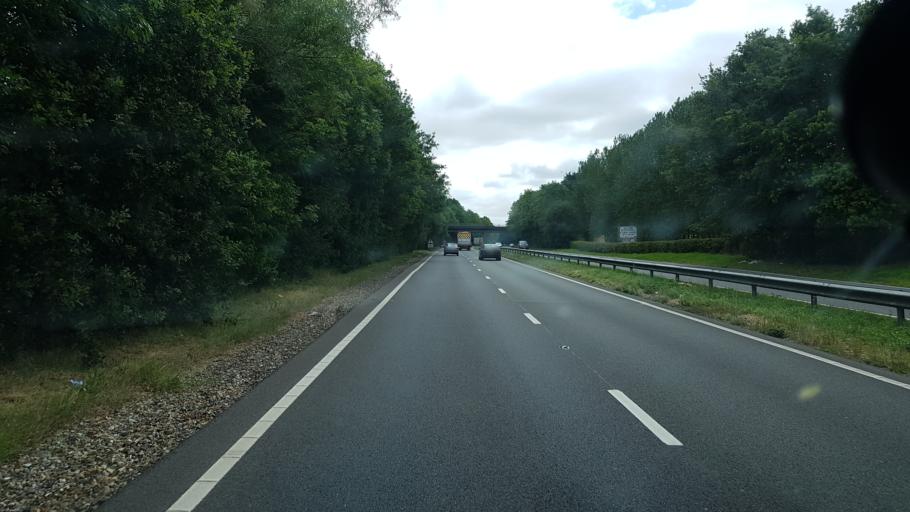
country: GB
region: England
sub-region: Surrey
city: Godstone
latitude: 51.2554
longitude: -0.0585
